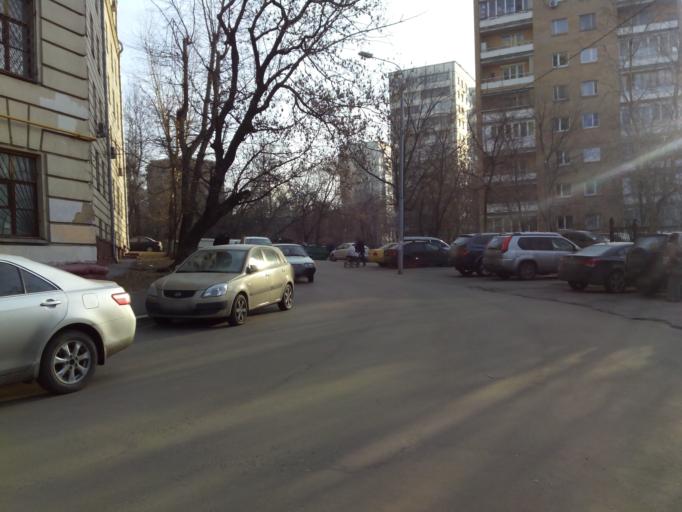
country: RU
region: Moscow
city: Lefortovo
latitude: 55.7739
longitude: 37.7037
